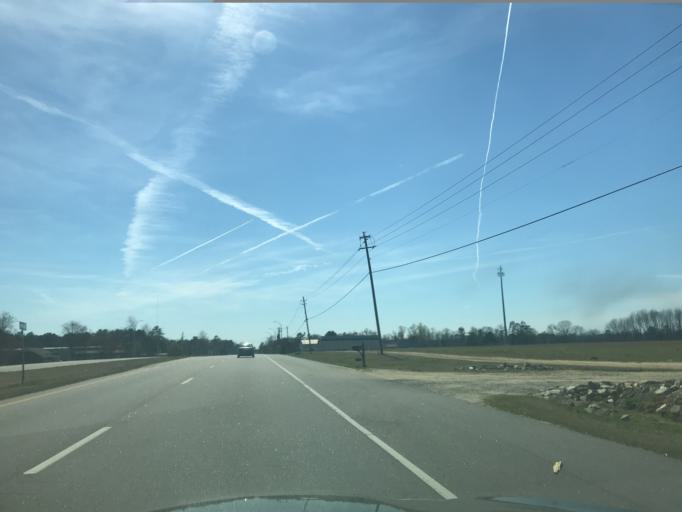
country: US
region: North Carolina
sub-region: Wake County
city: Fuquay-Varina
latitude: 35.6084
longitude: -78.7446
